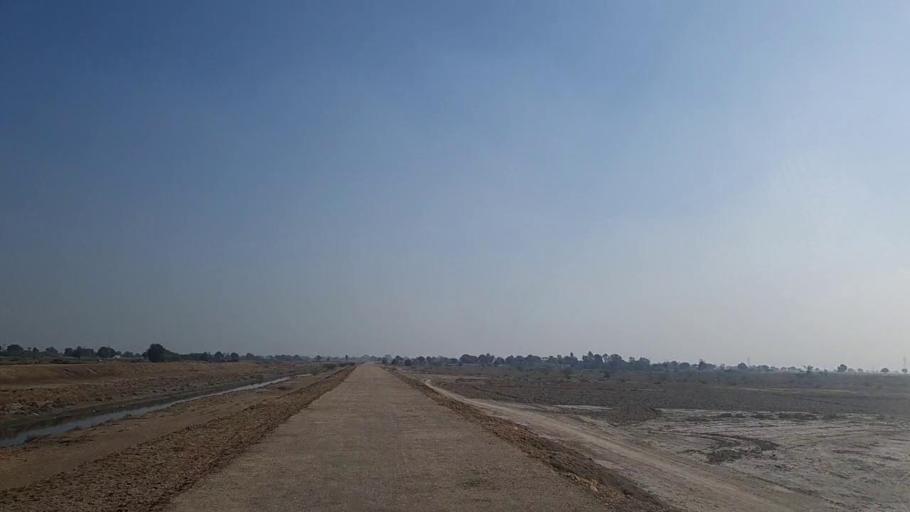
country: PK
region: Sindh
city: Shahpur Chakar
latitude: 26.1868
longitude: 68.5594
